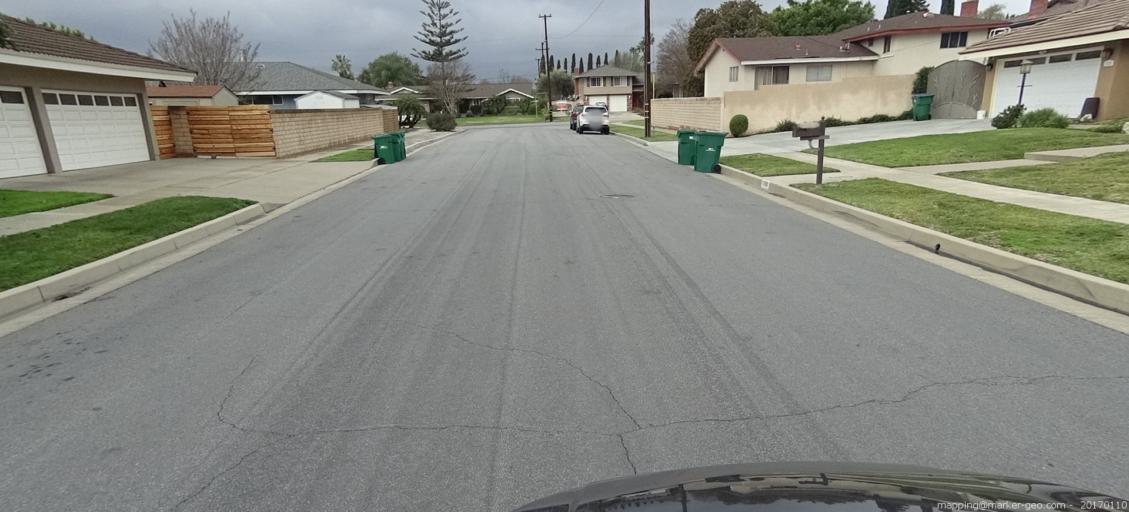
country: US
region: California
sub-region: Orange County
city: Tustin
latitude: 33.7695
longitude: -117.8223
